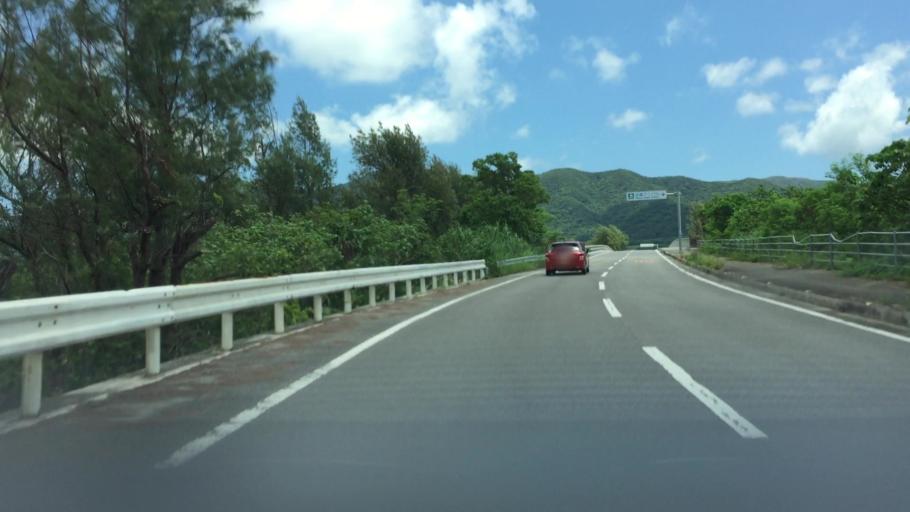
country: JP
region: Okinawa
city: Ishigaki
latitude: 24.4009
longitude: 124.1403
